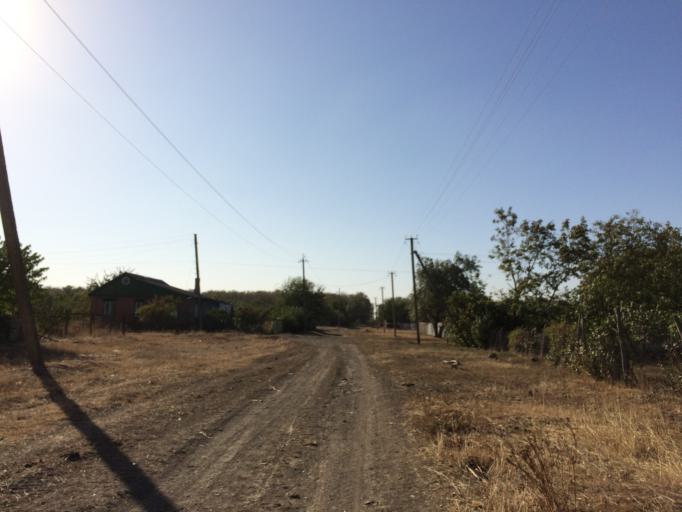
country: RU
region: Rostov
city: Tselina
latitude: 46.5246
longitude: 41.1866
